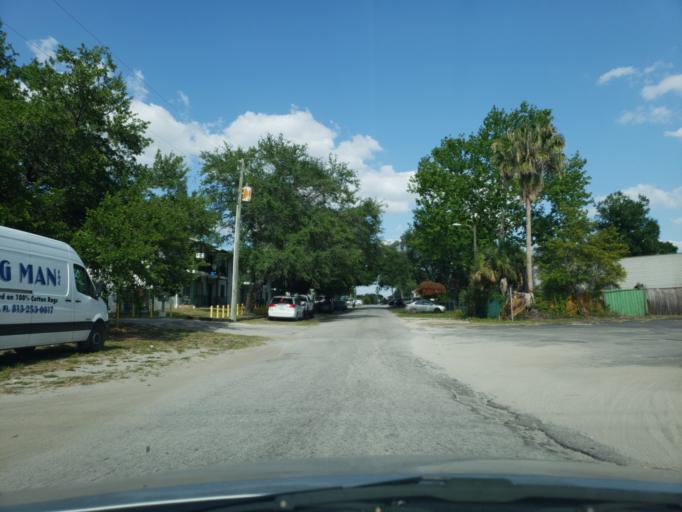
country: US
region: Florida
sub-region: Hillsborough County
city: Tampa
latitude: 27.9674
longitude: -82.4826
